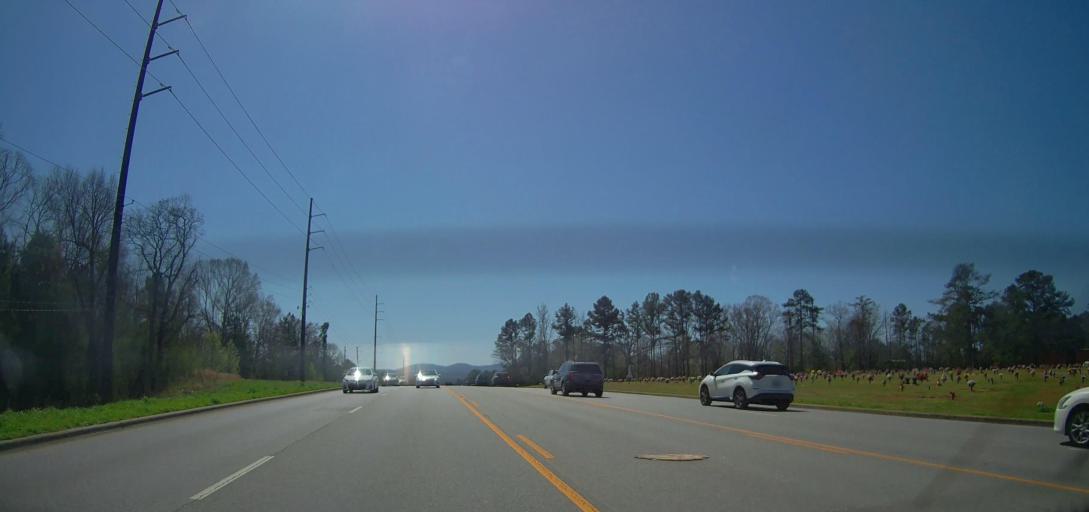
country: US
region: Alabama
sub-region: Calhoun County
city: Anniston
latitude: 33.6344
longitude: -85.7860
